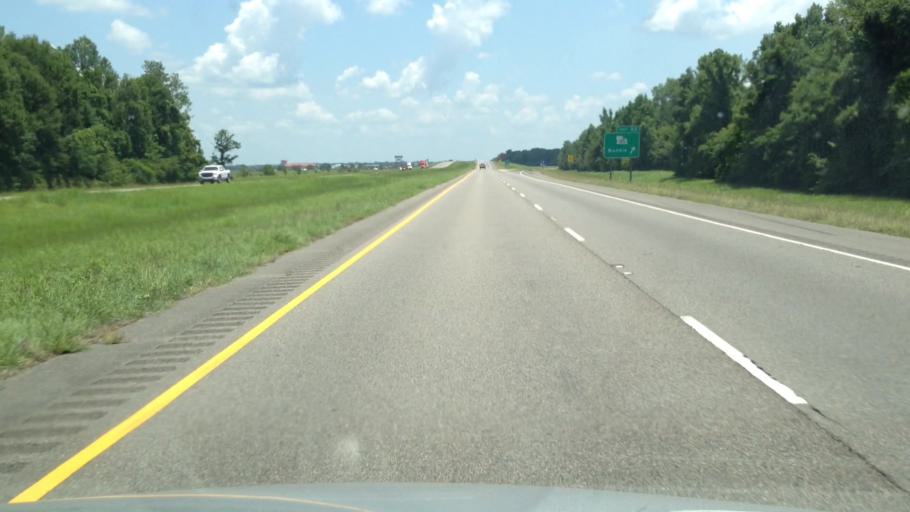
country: US
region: Louisiana
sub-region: Avoyelles Parish
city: Bunkie
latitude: 30.9577
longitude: -92.2811
